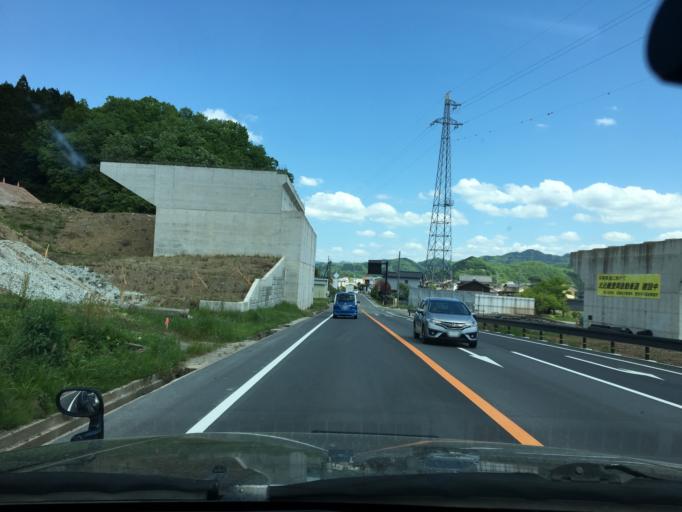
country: JP
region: Hyogo
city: Toyooka
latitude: 35.4688
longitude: 134.7625
